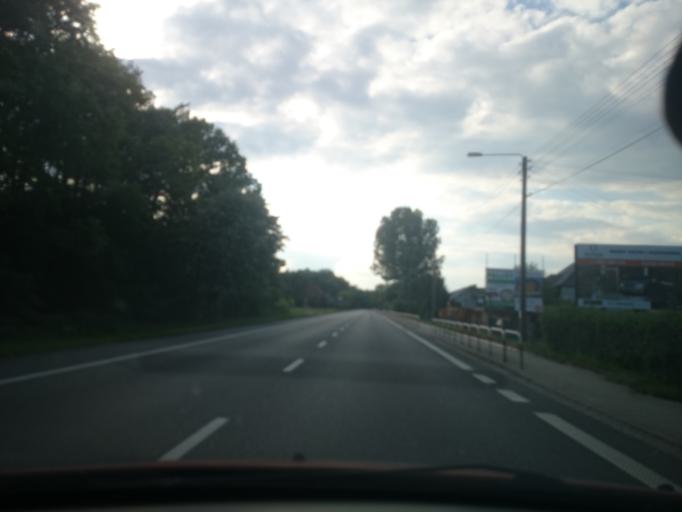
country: PL
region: Opole Voivodeship
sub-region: Powiat opolski
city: Tarnow Opolski
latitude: 50.6023
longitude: 18.0802
